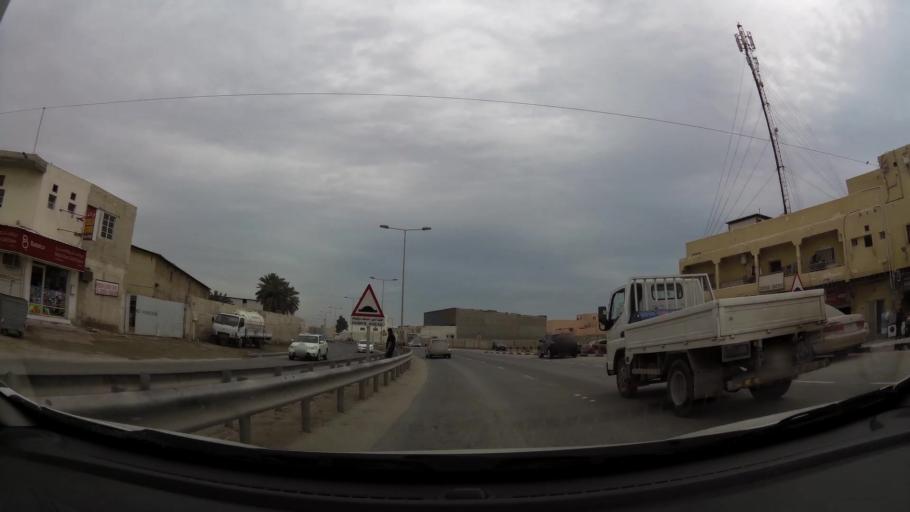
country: BH
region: Northern
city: Sitrah
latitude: 26.1537
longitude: 50.6206
